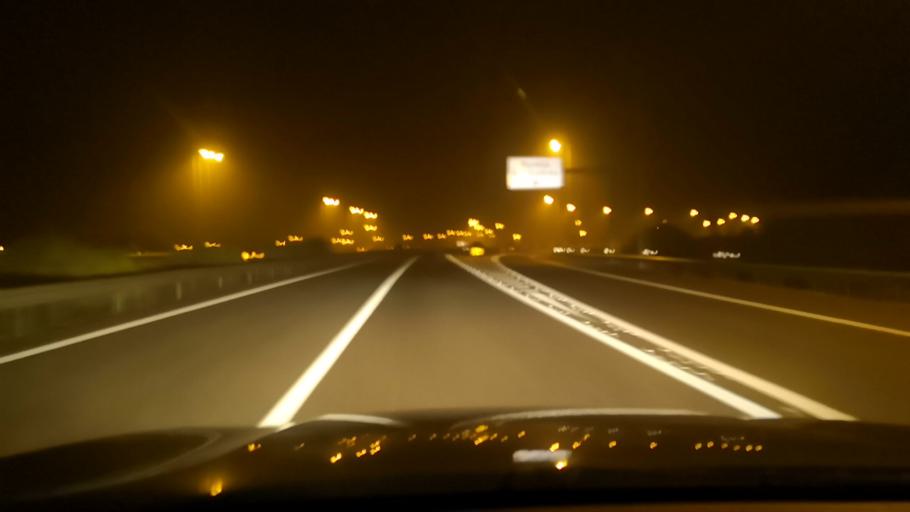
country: PT
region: Santarem
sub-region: Benavente
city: Poceirao
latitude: 38.8397
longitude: -8.7305
